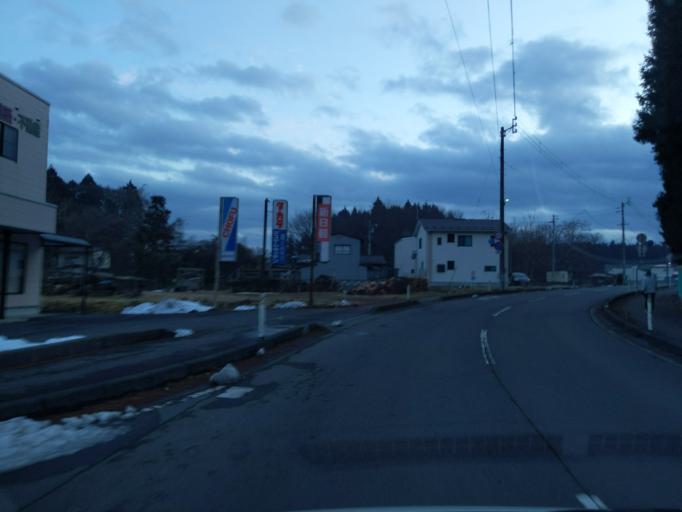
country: JP
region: Iwate
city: Mizusawa
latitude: 39.1243
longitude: 141.1416
